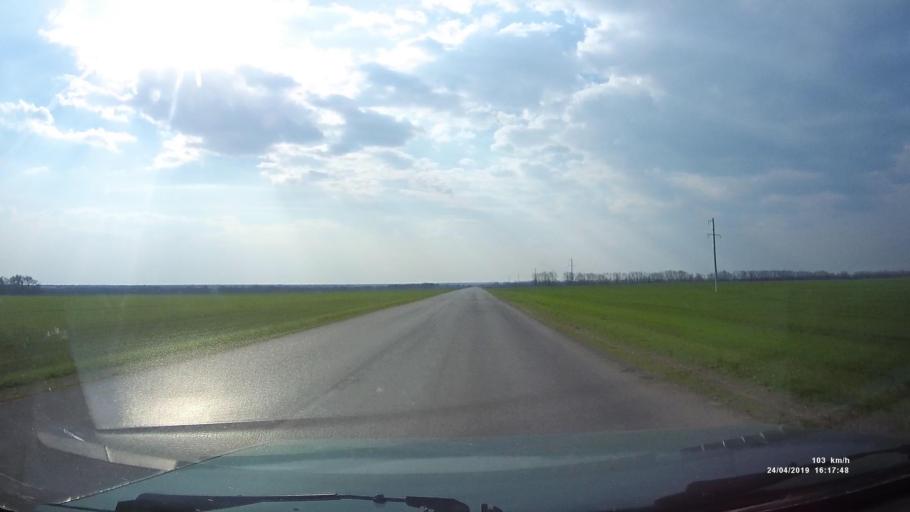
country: RU
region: Rostov
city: Sovetskoye
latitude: 46.7709
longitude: 42.1300
